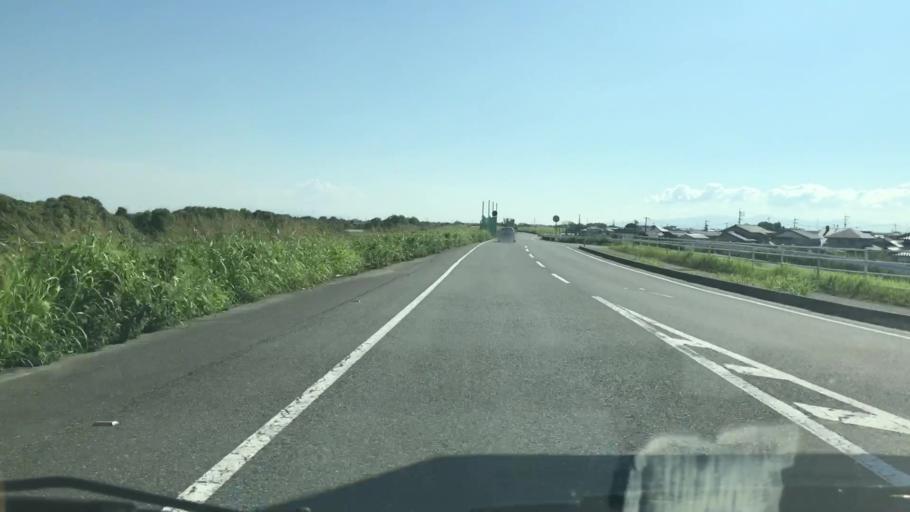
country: JP
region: Fukuoka
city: Kurume
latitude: 33.2828
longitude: 130.4495
